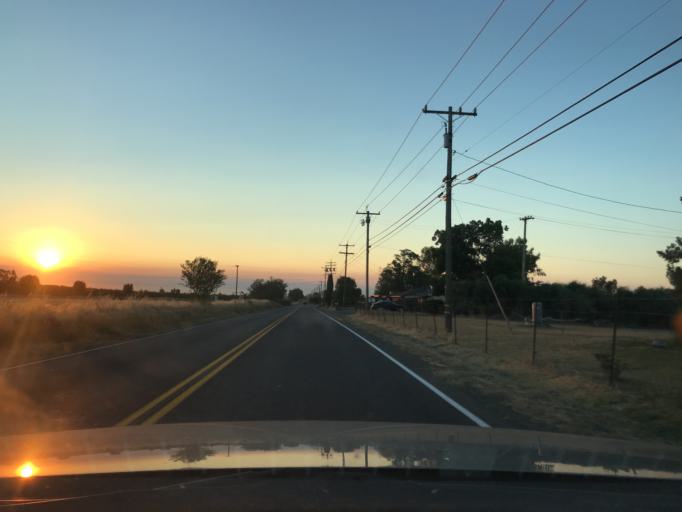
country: US
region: California
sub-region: Merced County
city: Merced
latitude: 37.3391
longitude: -120.5155
